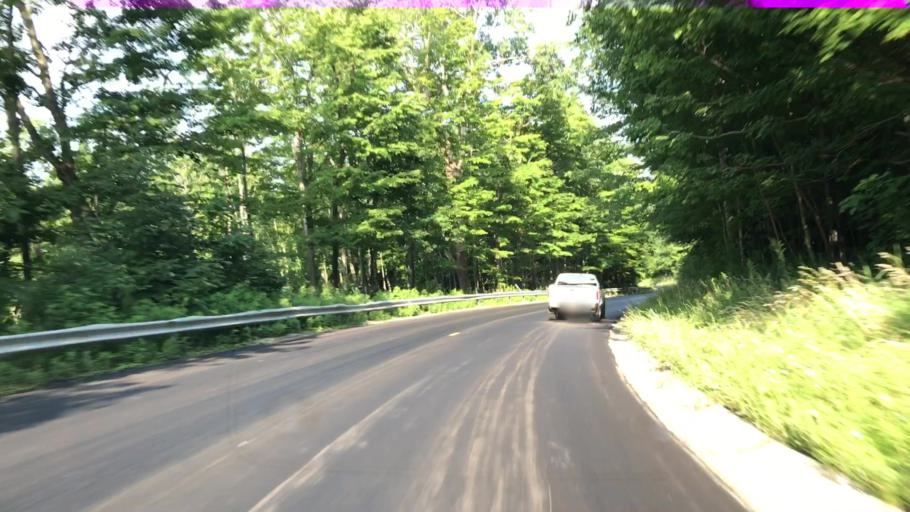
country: US
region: New York
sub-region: Chautauqua County
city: Brocton
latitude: 42.3184
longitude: -79.3490
